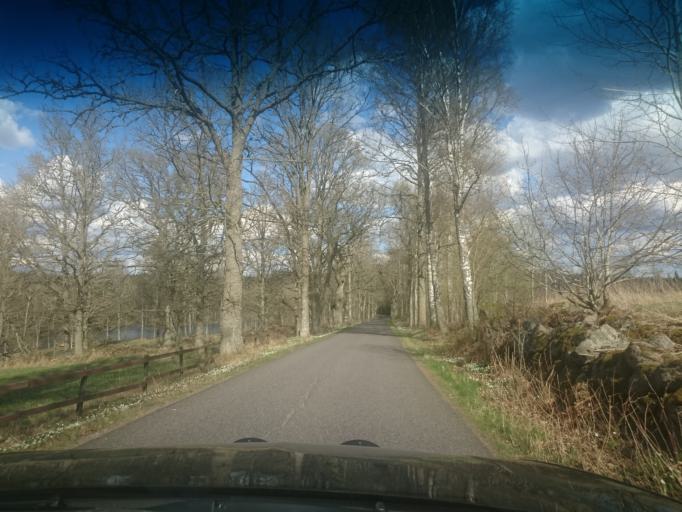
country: SE
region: Kronoberg
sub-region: Vaxjo Kommun
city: Braas
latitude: 57.1460
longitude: 15.1532
